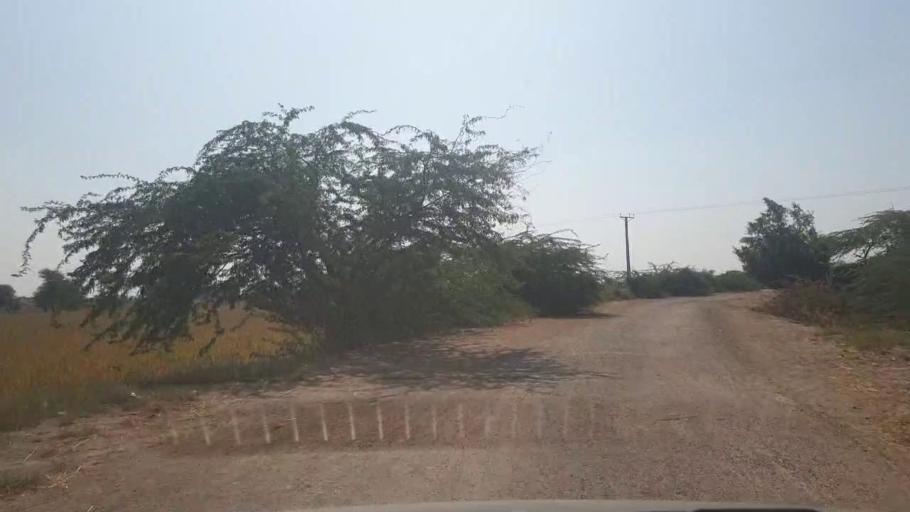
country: PK
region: Sindh
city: Badin
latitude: 24.5781
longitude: 68.8456
